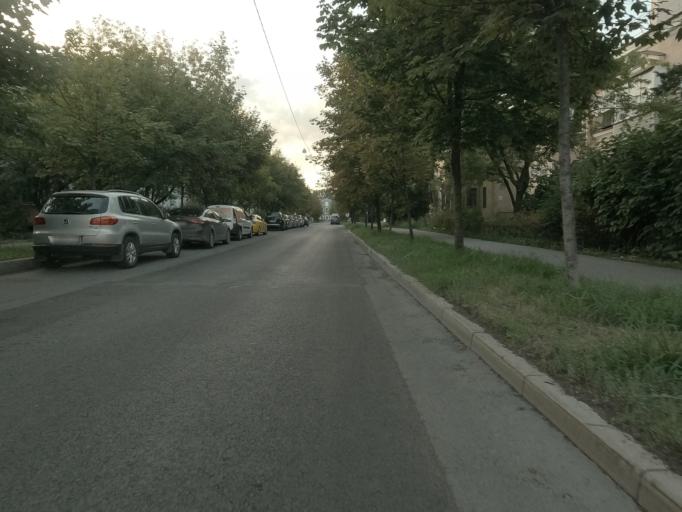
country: RU
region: St.-Petersburg
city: Avtovo
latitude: 59.8951
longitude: 30.2631
